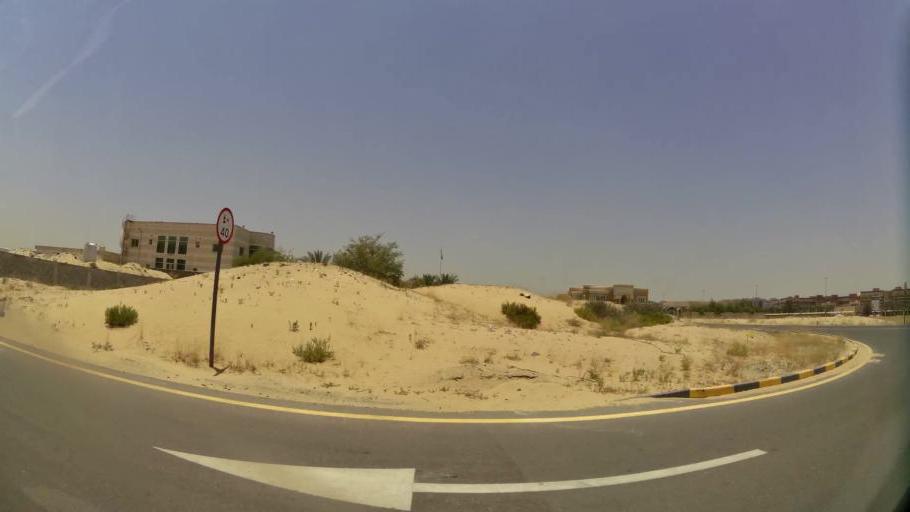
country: AE
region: Ajman
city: Ajman
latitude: 25.4068
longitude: 55.5074
